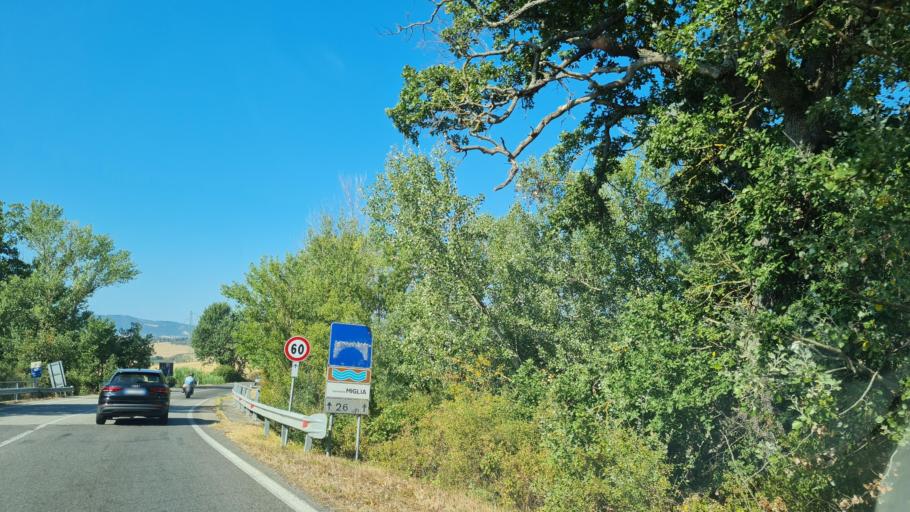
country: IT
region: Tuscany
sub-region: Provincia di Siena
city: Chianciano Terme
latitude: 43.0088
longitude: 11.7594
